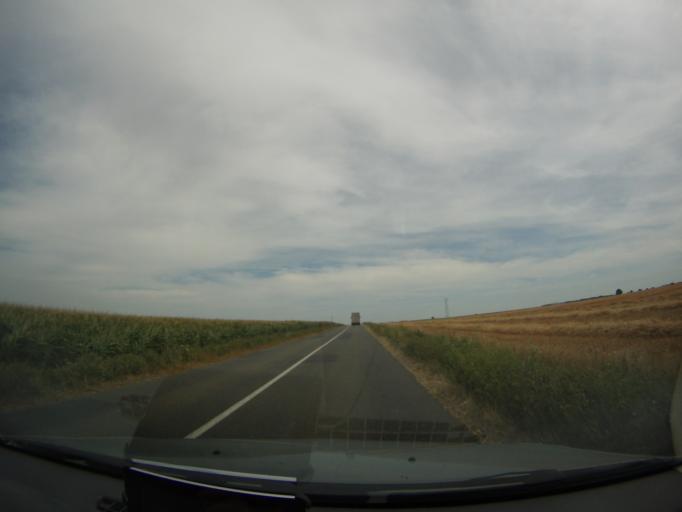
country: FR
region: Poitou-Charentes
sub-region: Departement de la Vienne
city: Mirebeau
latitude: 46.7307
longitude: 0.1947
